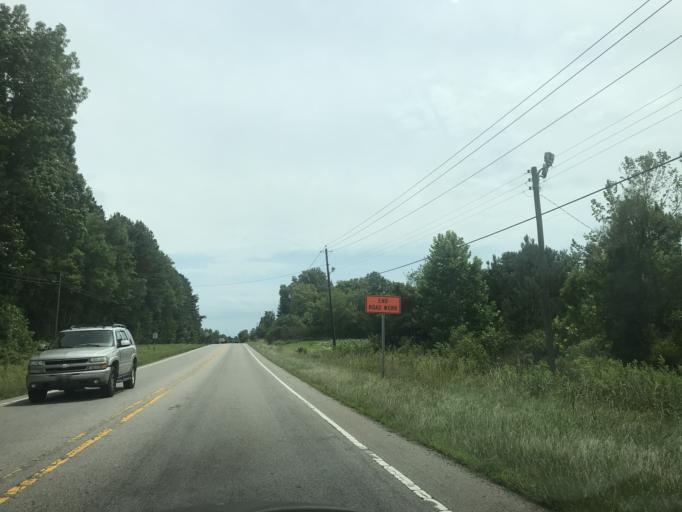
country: US
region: North Carolina
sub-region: Vance County
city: South Henderson
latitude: 36.2929
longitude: -78.4054
